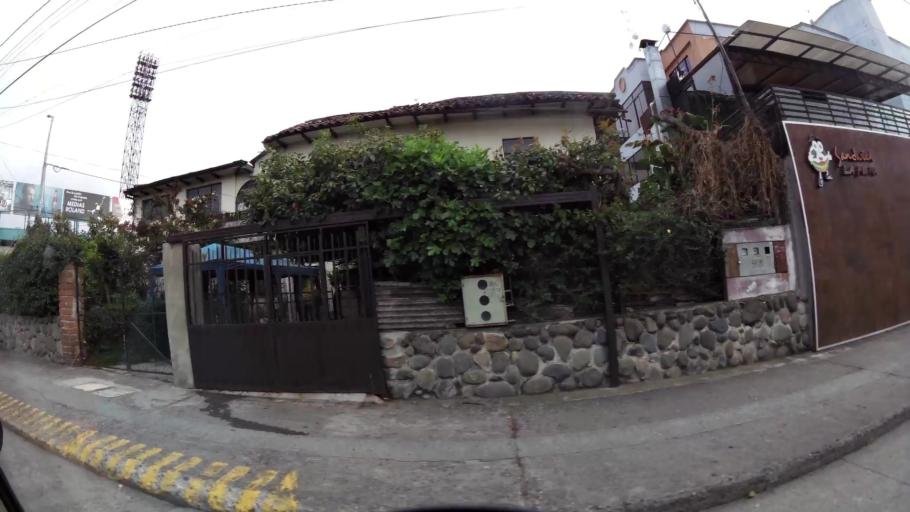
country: EC
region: Azuay
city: Cuenca
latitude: -2.9079
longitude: -79.0055
